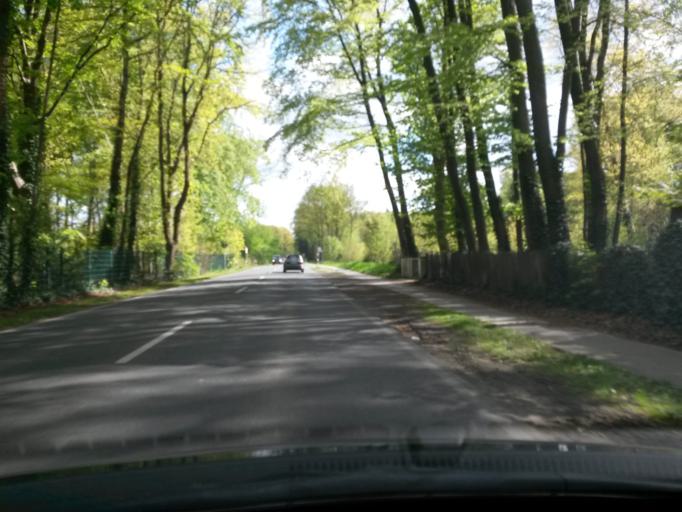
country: DE
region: North Rhine-Westphalia
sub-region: Regierungsbezirk Dusseldorf
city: Schwalmtal
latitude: 51.1955
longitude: 6.3400
